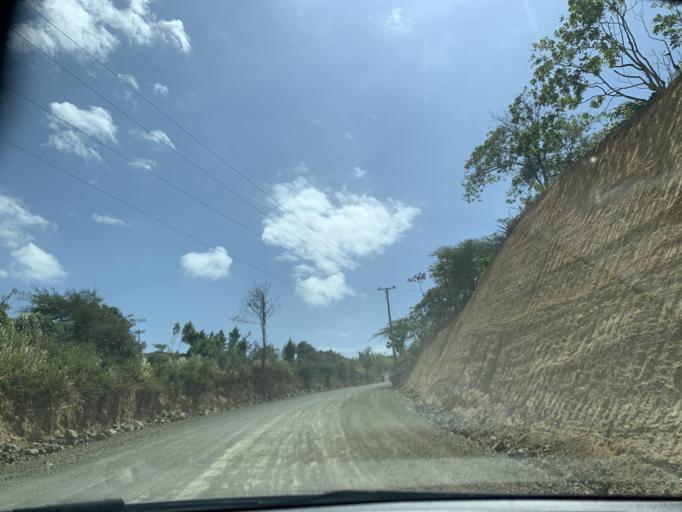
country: DO
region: Puerto Plata
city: Luperon
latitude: 19.8808
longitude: -70.8516
